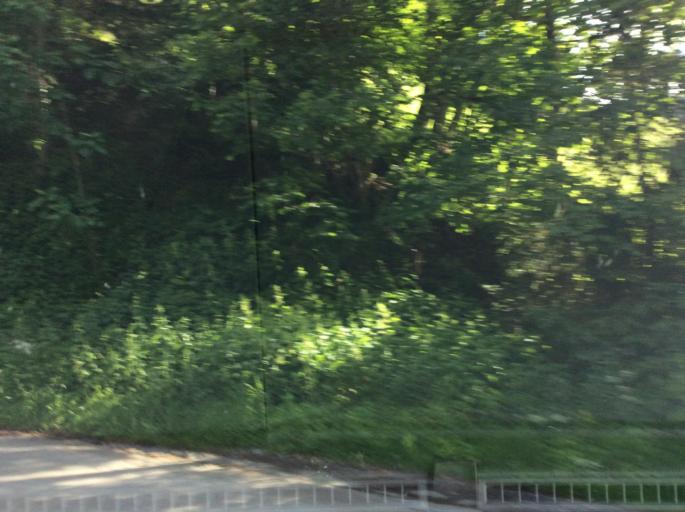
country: AT
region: Salzburg
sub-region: Politischer Bezirk Sankt Johann im Pongau
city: Forstau
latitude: 47.4082
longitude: 13.5911
